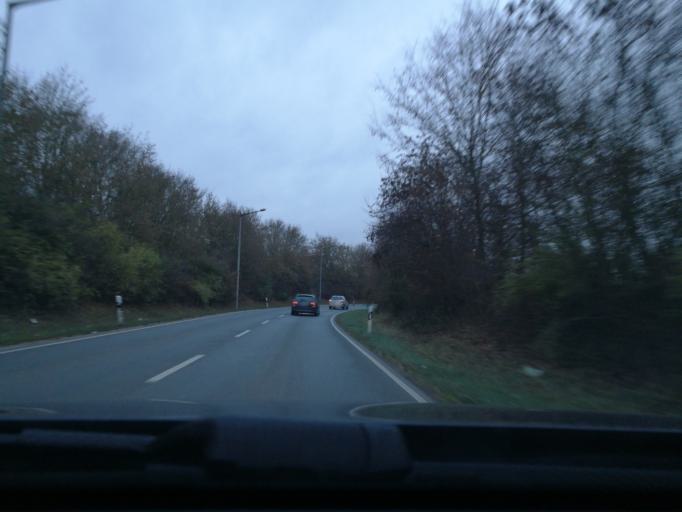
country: DE
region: Bavaria
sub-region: Regierungsbezirk Mittelfranken
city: Furth
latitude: 49.4699
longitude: 10.9631
